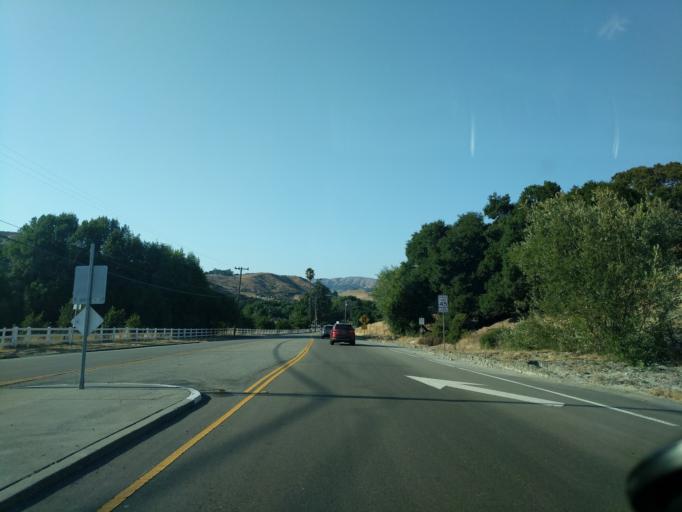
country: US
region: California
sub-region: Contra Costa County
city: San Ramon
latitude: 37.7467
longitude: -122.0313
